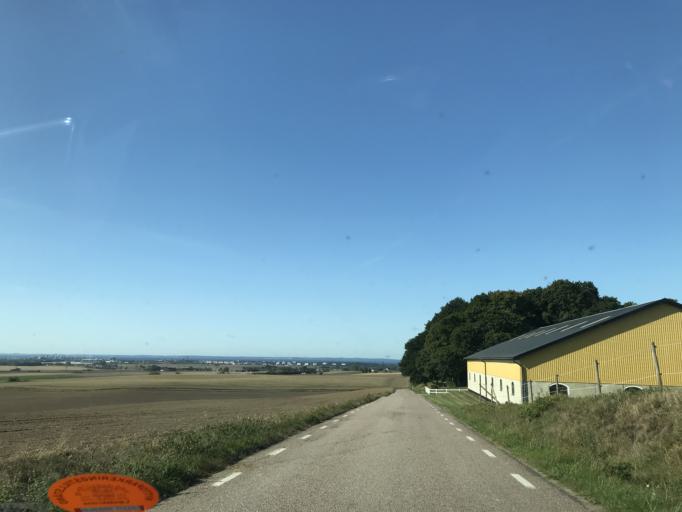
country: SE
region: Skane
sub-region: Landskrona
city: Asmundtorp
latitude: 55.9061
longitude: 12.9284
